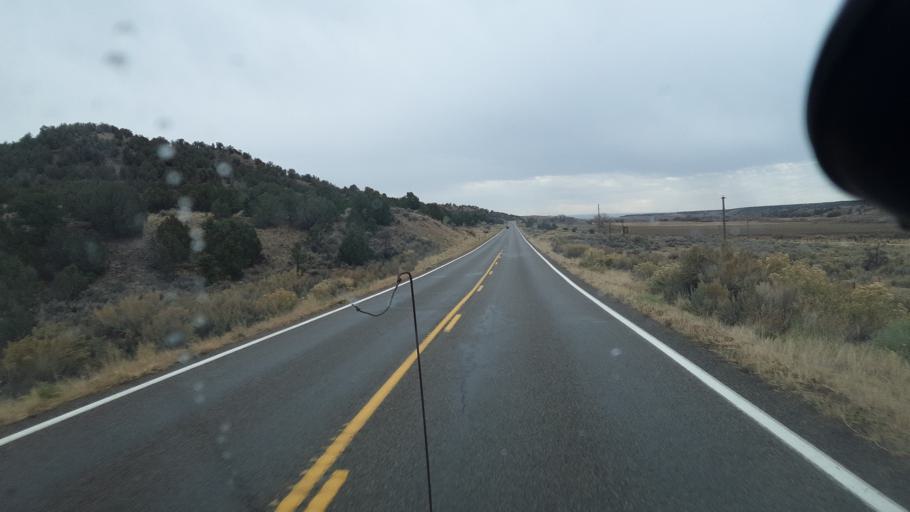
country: US
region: New Mexico
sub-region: San Juan County
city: Spencerville
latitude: 37.0363
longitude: -108.1822
